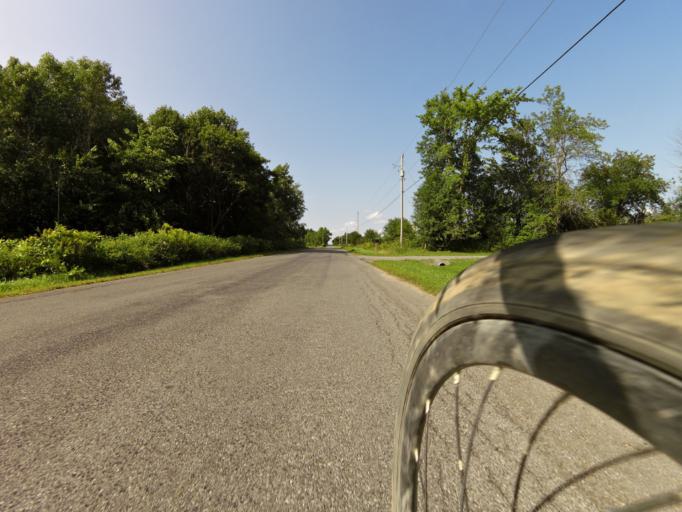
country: CA
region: Ontario
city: Kingston
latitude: 44.3136
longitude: -76.6716
